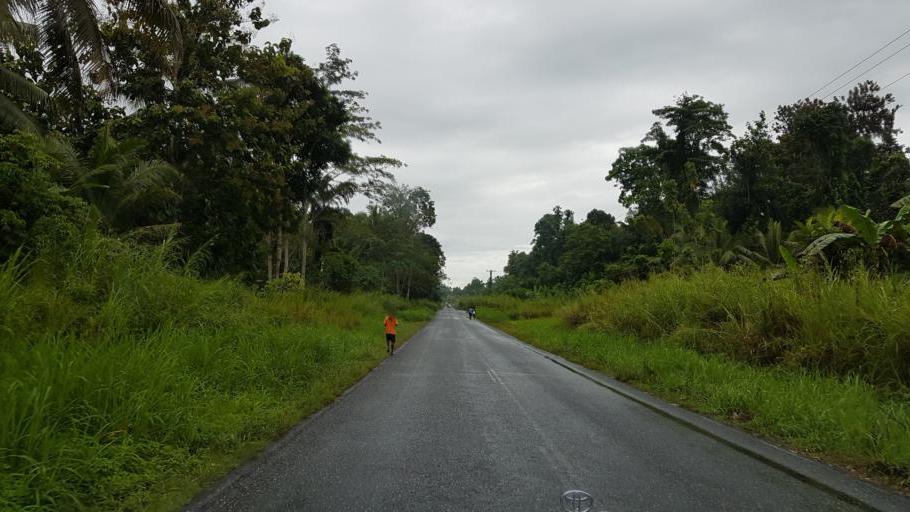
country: PG
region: Northern Province
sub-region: Sohe
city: Popondetta
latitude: -8.7969
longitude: 148.2281
